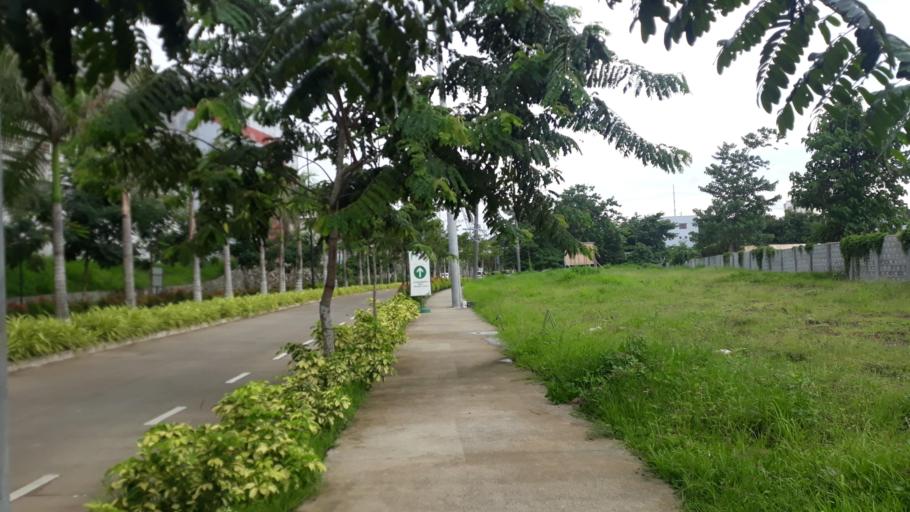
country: PH
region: Calabarzon
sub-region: Province of Cavite
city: Dasmarinas
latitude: 14.3010
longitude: 120.9491
